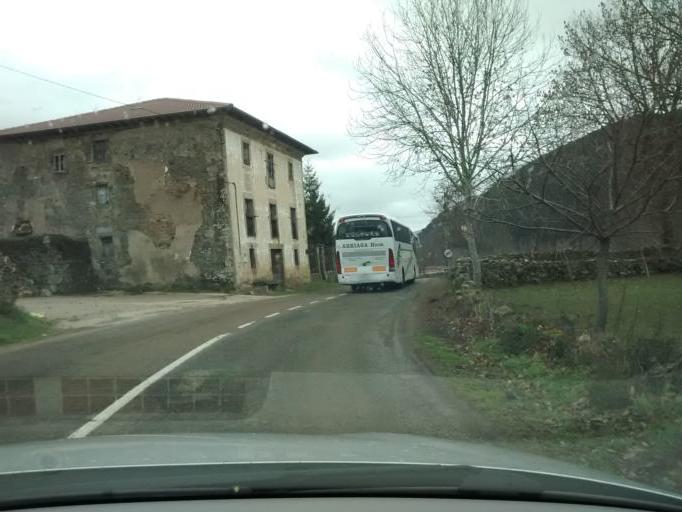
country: ES
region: Castille and Leon
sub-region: Provincia de Burgos
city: Espinosa de los Monteros
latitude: 43.0971
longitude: -3.5644
